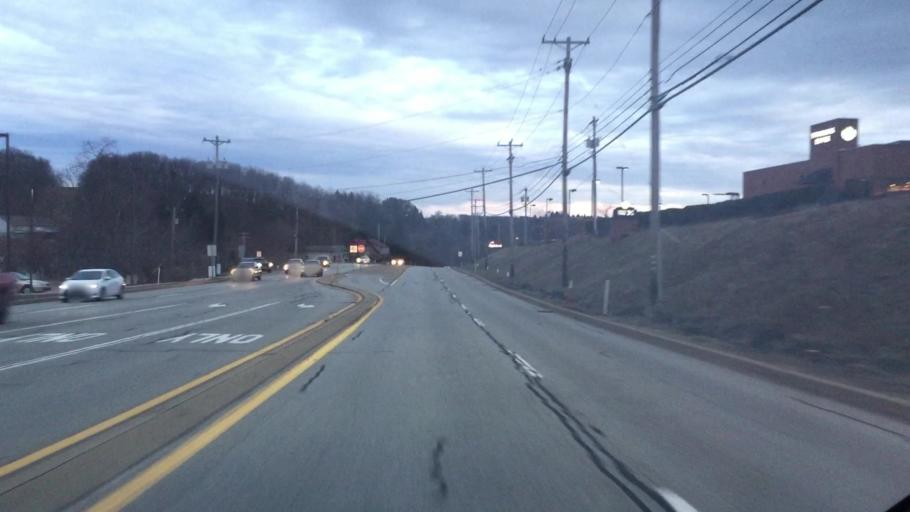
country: US
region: Pennsylvania
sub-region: Allegheny County
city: Bakerstown
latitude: 40.6414
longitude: -79.9384
